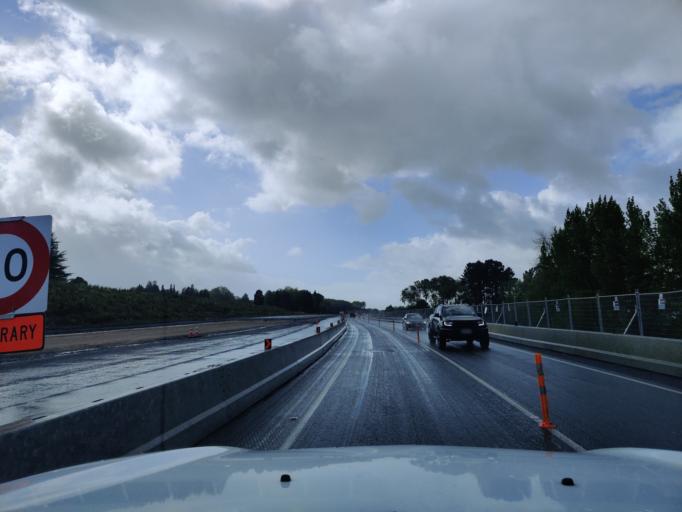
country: NZ
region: Waikato
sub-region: Hamilton City
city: Hamilton
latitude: -37.8186
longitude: 175.3442
